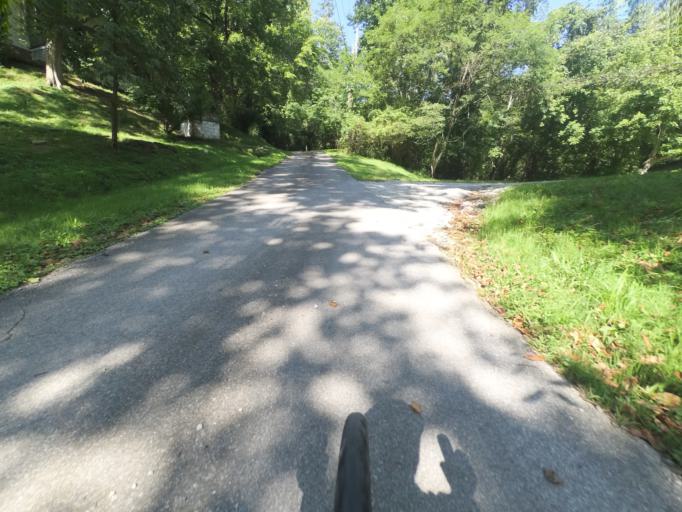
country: US
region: West Virginia
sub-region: Cabell County
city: Huntington
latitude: 38.3867
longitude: -82.4710
